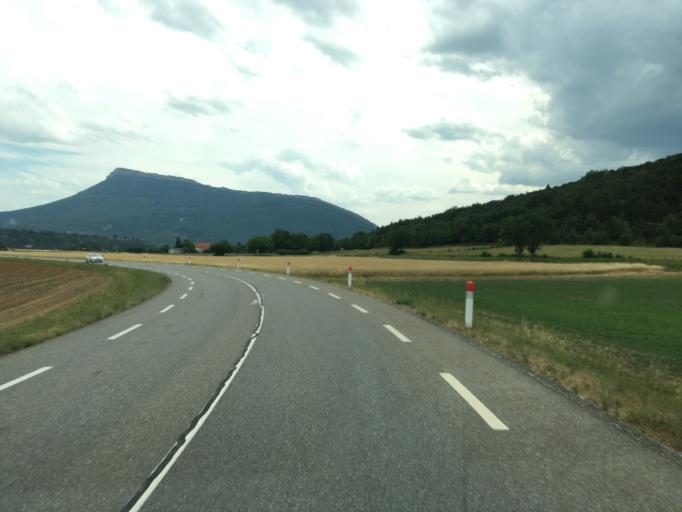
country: FR
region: Provence-Alpes-Cote d'Azur
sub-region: Departement des Hautes-Alpes
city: Serres
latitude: 44.4782
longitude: 5.7584
